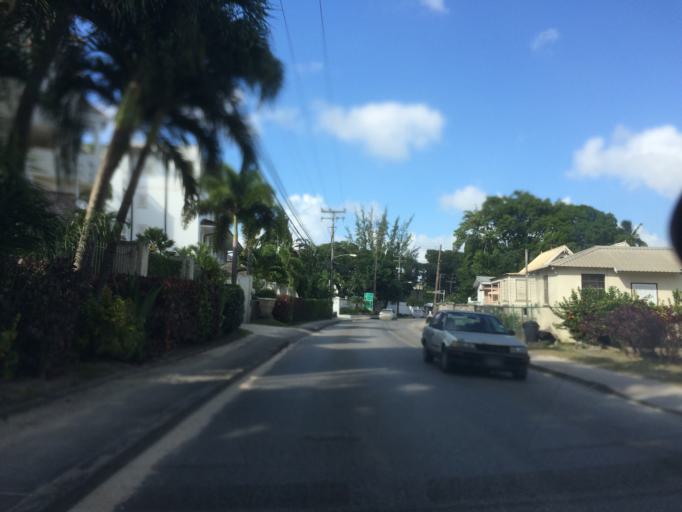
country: BB
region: Saint James
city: Holetown
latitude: 13.1604
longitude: -59.6373
